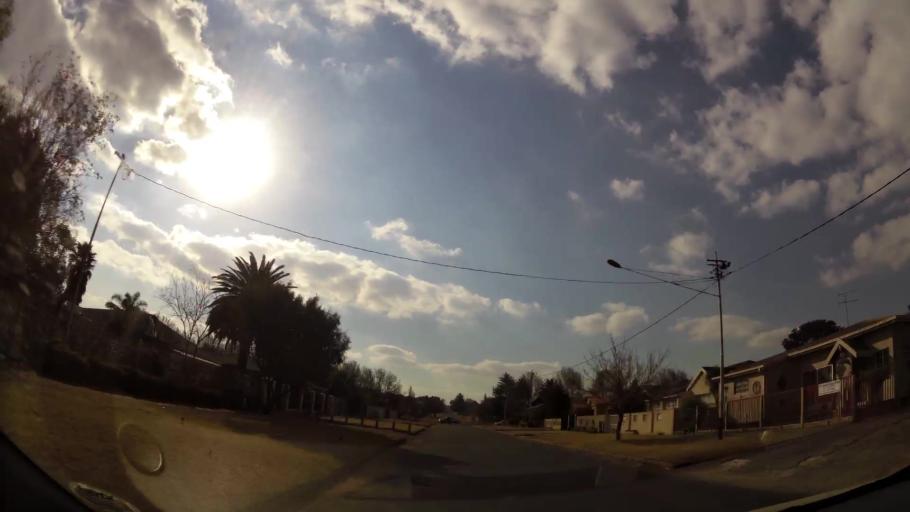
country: ZA
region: Gauteng
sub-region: West Rand District Municipality
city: Krugersdorp
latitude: -26.0894
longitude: 27.7657
